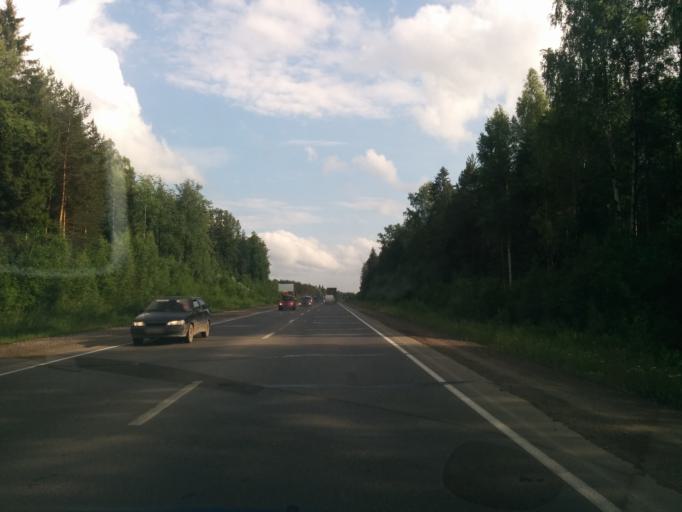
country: RU
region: Perm
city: Polazna
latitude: 58.1196
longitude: 56.4249
